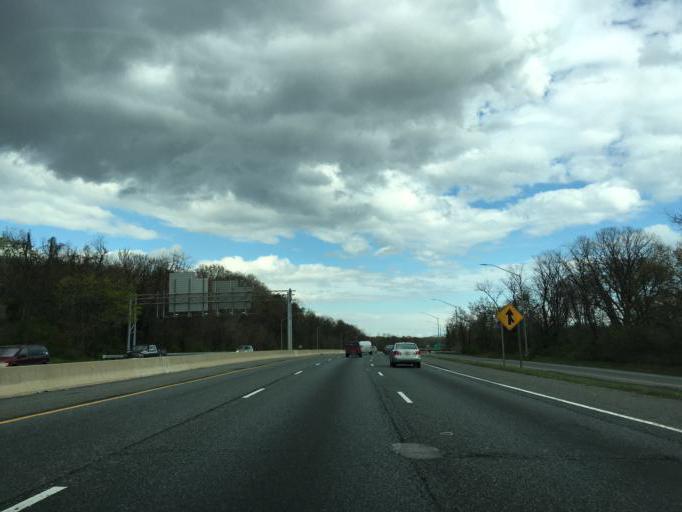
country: US
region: Maryland
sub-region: Anne Arundel County
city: Pumphrey
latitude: 39.2054
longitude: -76.6211
